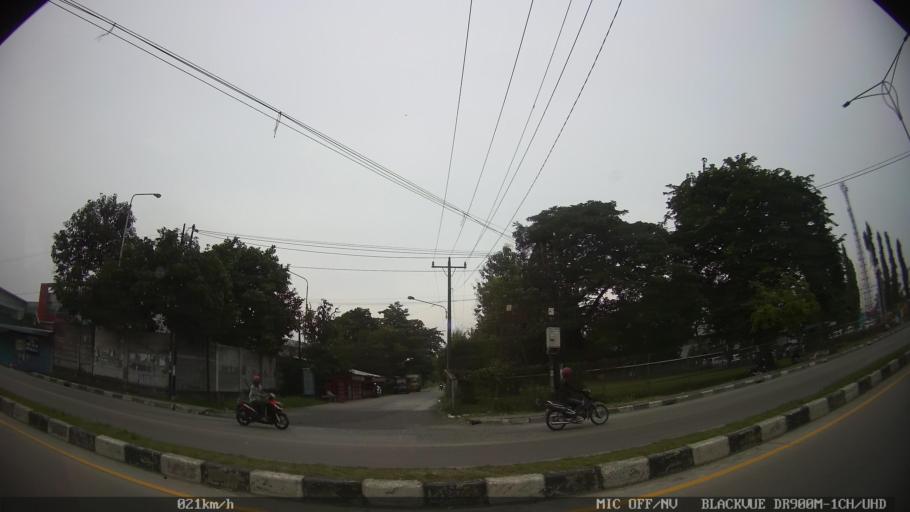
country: ID
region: North Sumatra
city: Deli Tua
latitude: 3.5326
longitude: 98.7261
